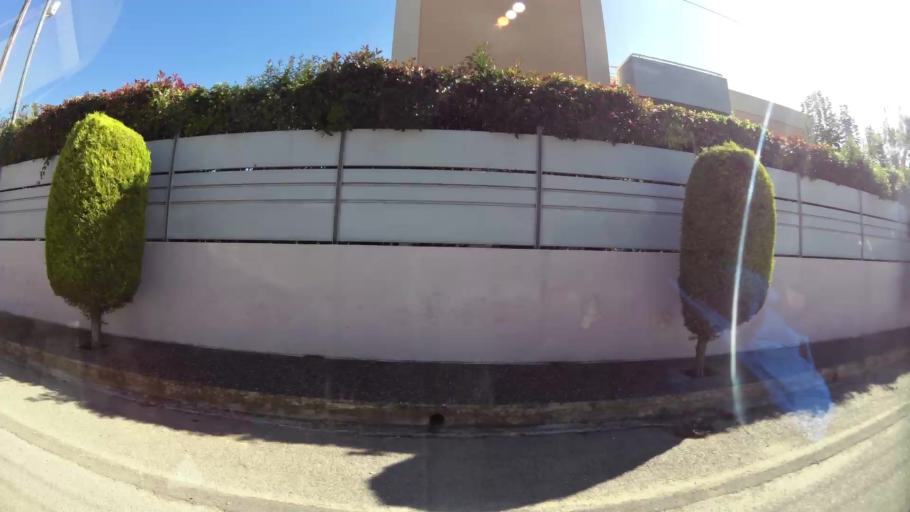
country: GR
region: Attica
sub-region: Nomarchia Athinas
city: Ekali
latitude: 38.1036
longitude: 23.8272
